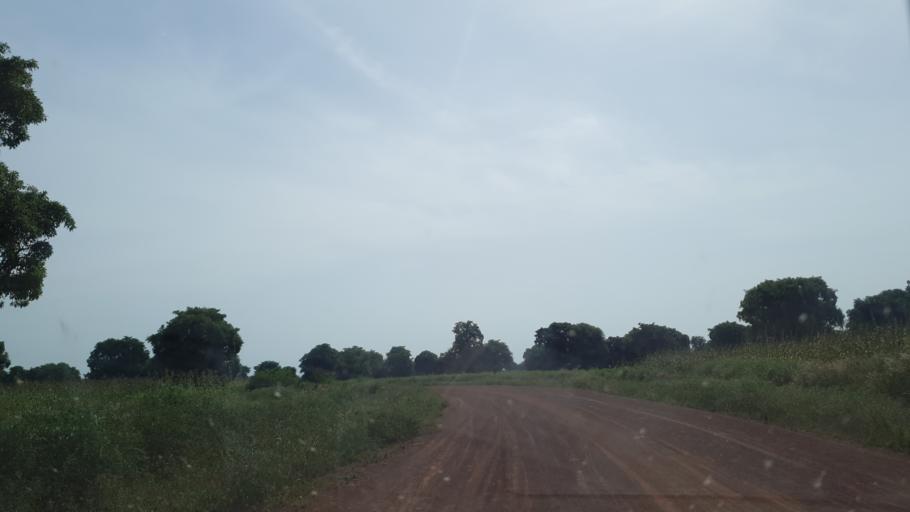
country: ML
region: Koulikoro
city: Dioila
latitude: 12.4119
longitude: -6.2505
